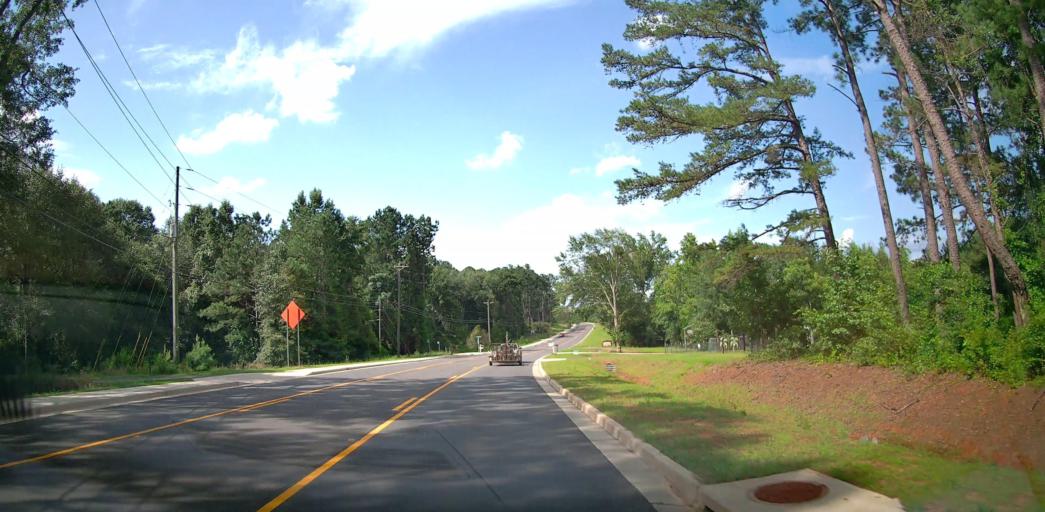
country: US
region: Georgia
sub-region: Houston County
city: Perry
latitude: 32.5020
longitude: -83.6992
